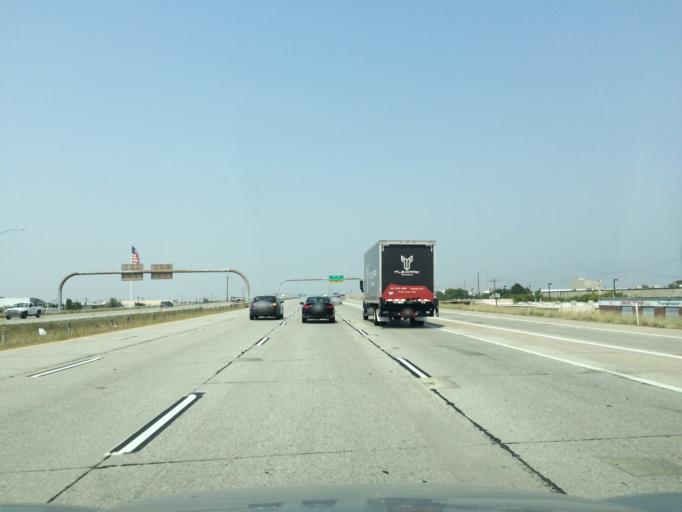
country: US
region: Utah
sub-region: Salt Lake County
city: South Salt Lake
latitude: 40.7298
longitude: -111.9500
